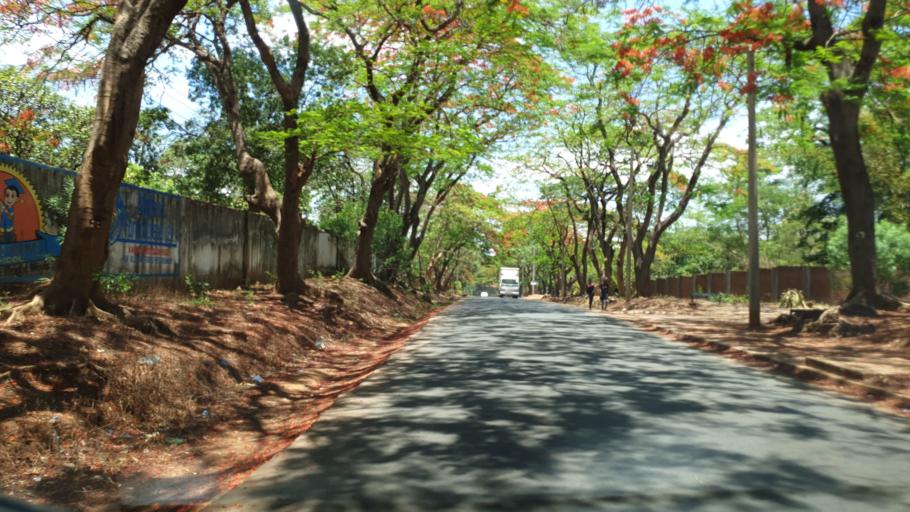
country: MW
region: Central Region
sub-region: Lilongwe District
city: Lilongwe
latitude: -13.9870
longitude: 33.7590
